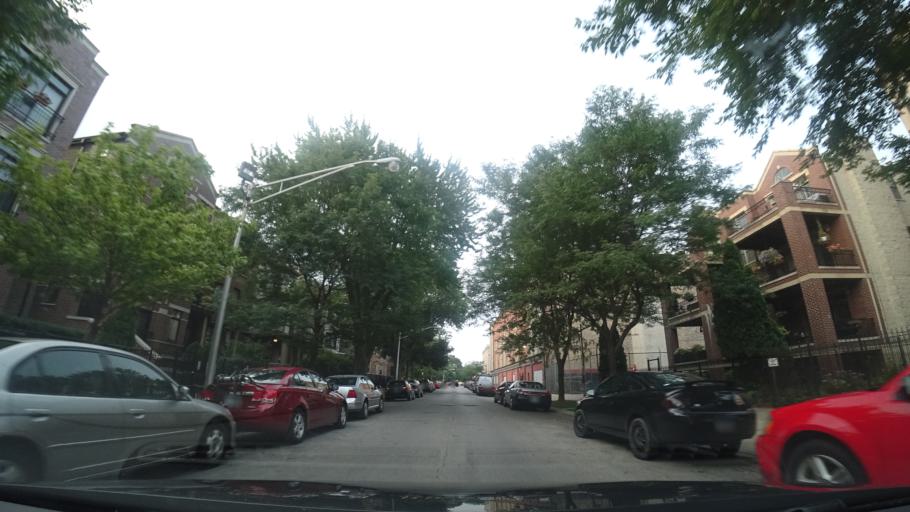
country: US
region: Illinois
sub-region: Cook County
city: Evanston
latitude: 41.9701
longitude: -87.6577
